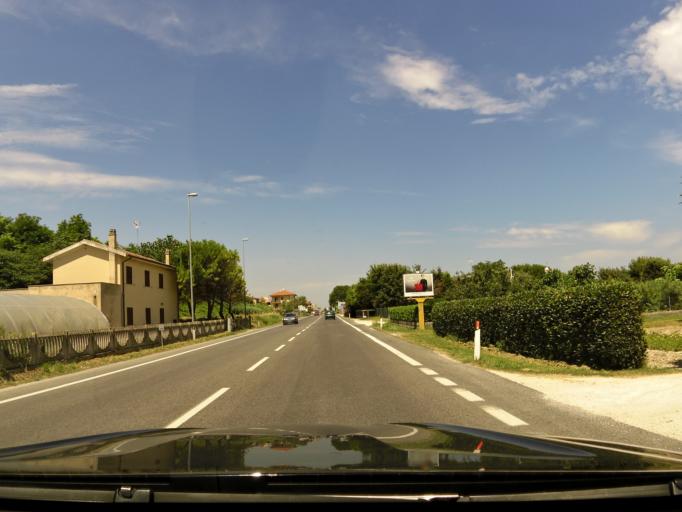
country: IT
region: The Marches
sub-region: Provincia di Pesaro e Urbino
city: Marotta
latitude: 43.7527
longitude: 13.1635
